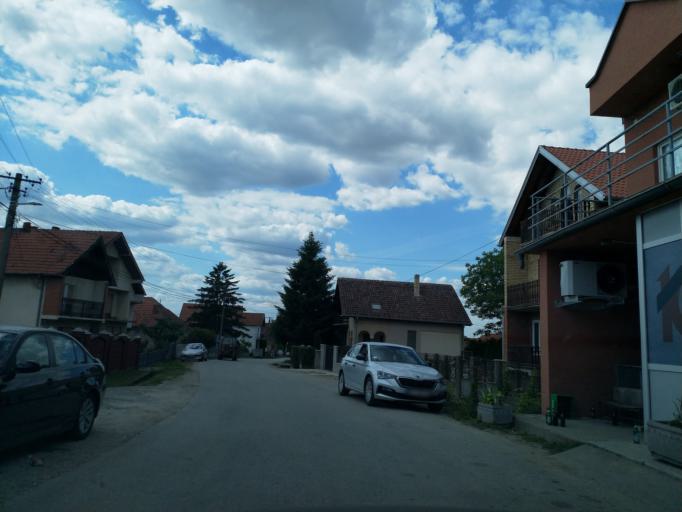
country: RS
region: Central Serbia
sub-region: Pomoravski Okrug
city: Jagodina
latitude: 43.9466
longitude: 21.2962
